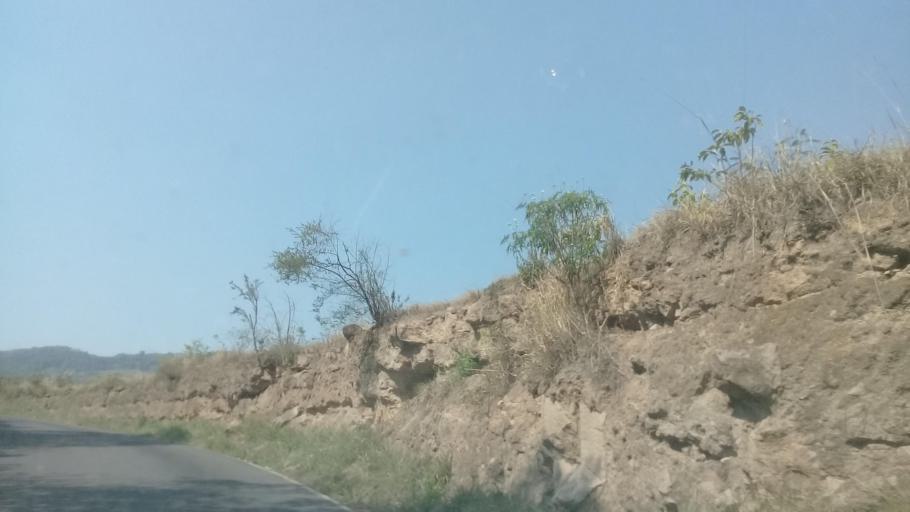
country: MX
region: Veracruz
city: El Castillo
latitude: 19.5763
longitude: -96.8321
